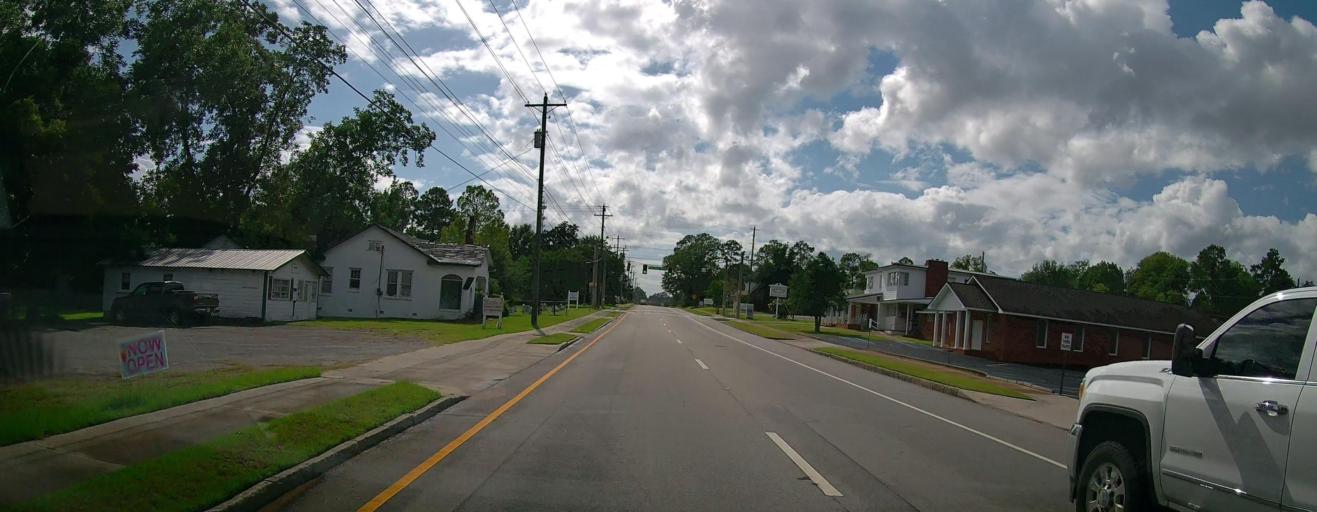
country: US
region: Georgia
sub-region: Coffee County
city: Douglas
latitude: 31.5090
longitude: -82.8535
